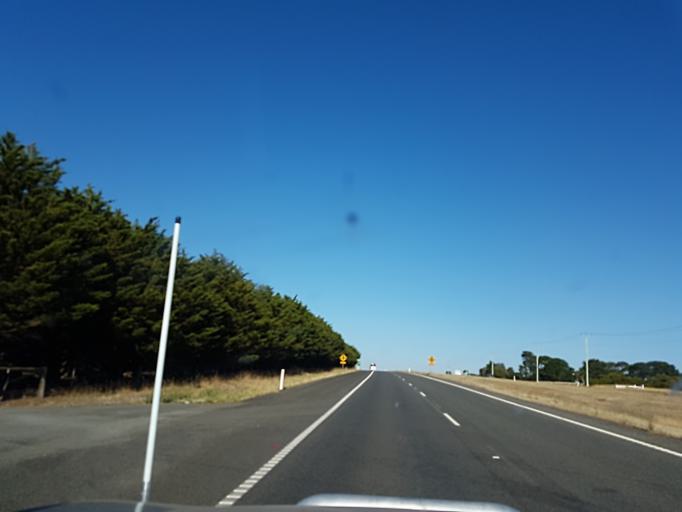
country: AU
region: Victoria
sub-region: Greater Geelong
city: Wandana Heights
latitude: -38.2122
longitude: 144.2110
